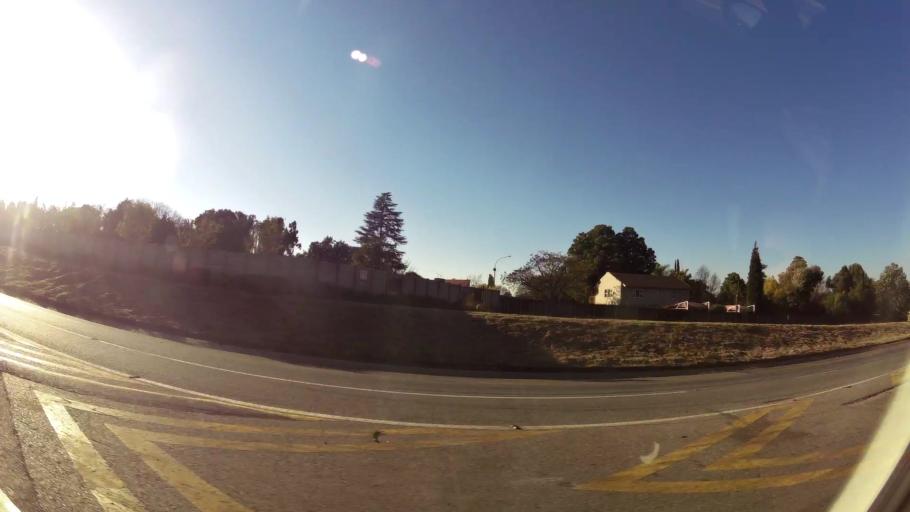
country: ZA
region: Gauteng
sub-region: Ekurhuleni Metropolitan Municipality
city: Germiston
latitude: -26.2826
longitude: 28.1019
